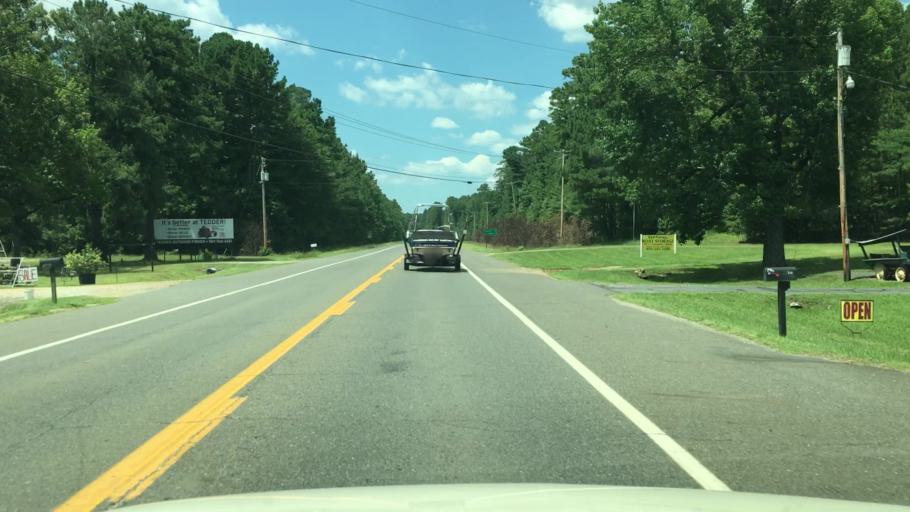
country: US
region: Arkansas
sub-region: Clark County
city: Arkadelphia
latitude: 34.1900
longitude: -93.0727
